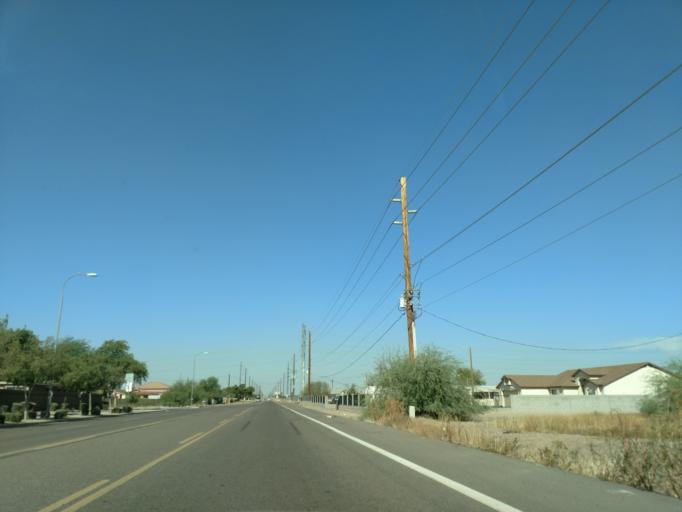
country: US
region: Arizona
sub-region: Maricopa County
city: Laveen
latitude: 33.4129
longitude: -112.1865
